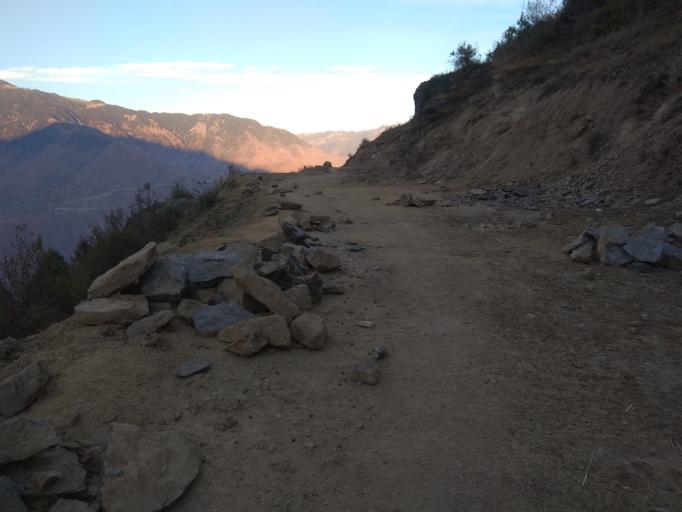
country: NP
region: Mid Western
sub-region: Karnali Zone
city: Jumla
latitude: 29.3140
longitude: 81.7285
